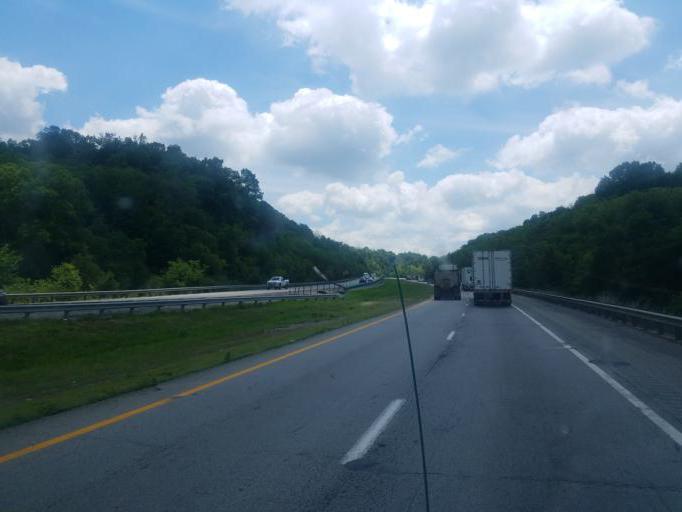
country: US
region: Kentucky
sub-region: Trimble County
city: Providence
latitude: 38.5917
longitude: -85.1757
